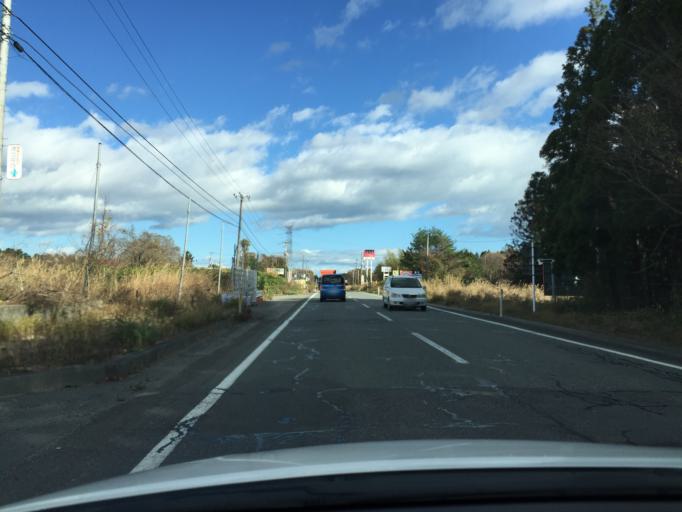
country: JP
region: Fukushima
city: Namie
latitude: 37.4205
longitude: 141.0022
